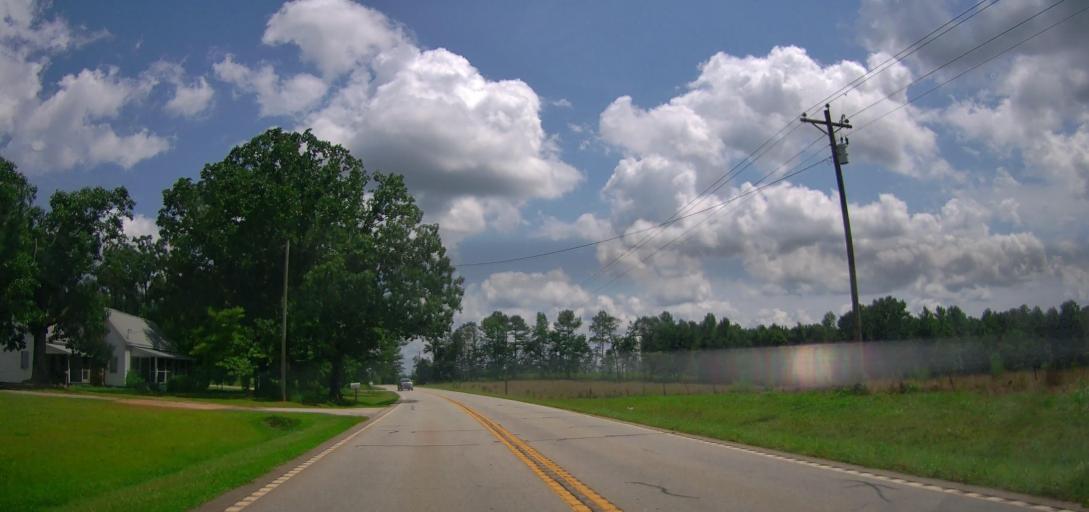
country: US
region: Georgia
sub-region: Heard County
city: Franklin
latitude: 33.3386
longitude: -85.1664
